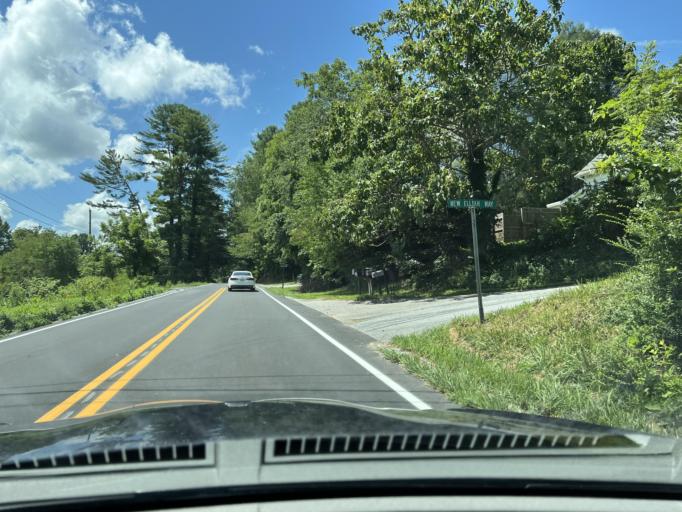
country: US
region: North Carolina
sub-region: Buncombe County
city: Fairview
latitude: 35.5009
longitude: -82.4218
